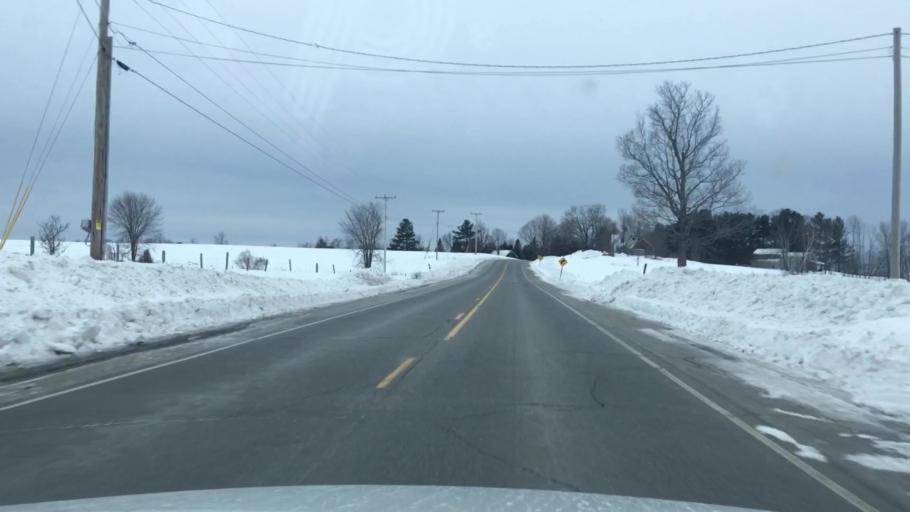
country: US
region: Maine
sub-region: Penobscot County
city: Corinna
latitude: 44.9311
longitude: -69.2382
